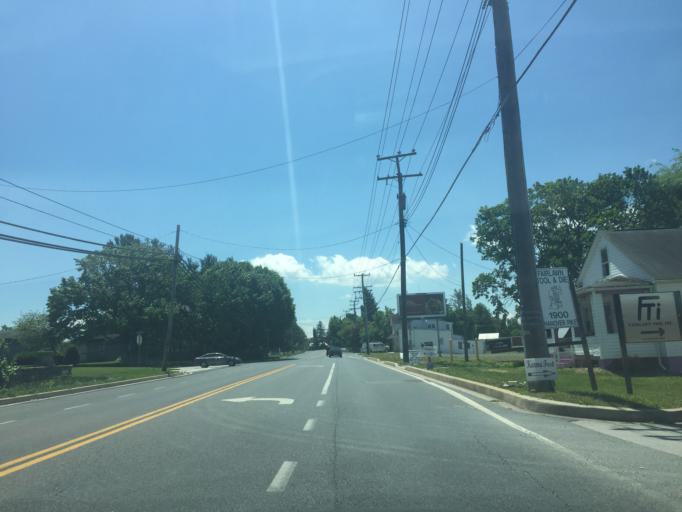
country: US
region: Maryland
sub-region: Carroll County
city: Hampstead
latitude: 39.6250
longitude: -76.8597
